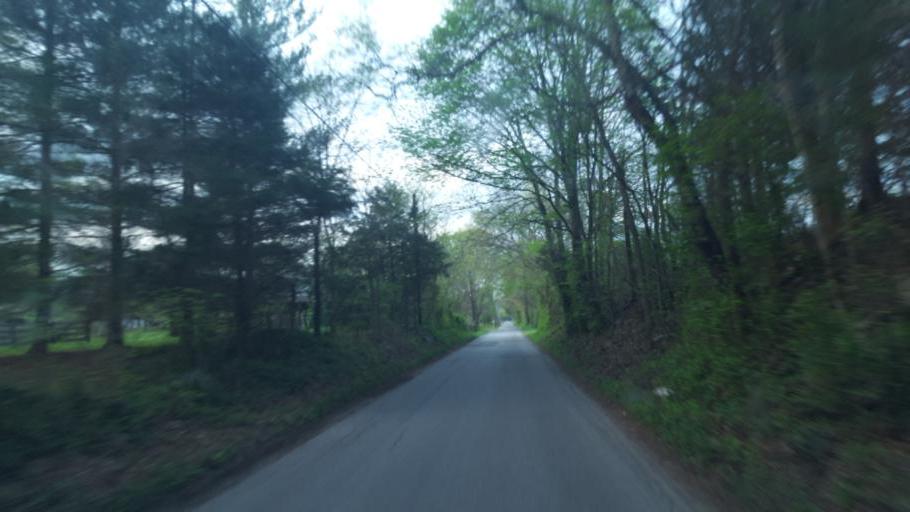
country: US
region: Kentucky
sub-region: Hart County
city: Munfordville
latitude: 37.2814
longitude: -85.9032
